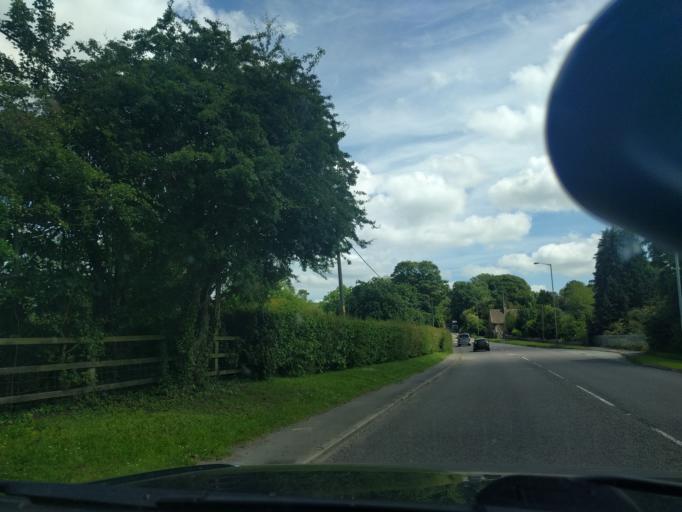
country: GB
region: England
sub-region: Wiltshire
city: Box
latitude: 51.4149
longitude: -2.2613
